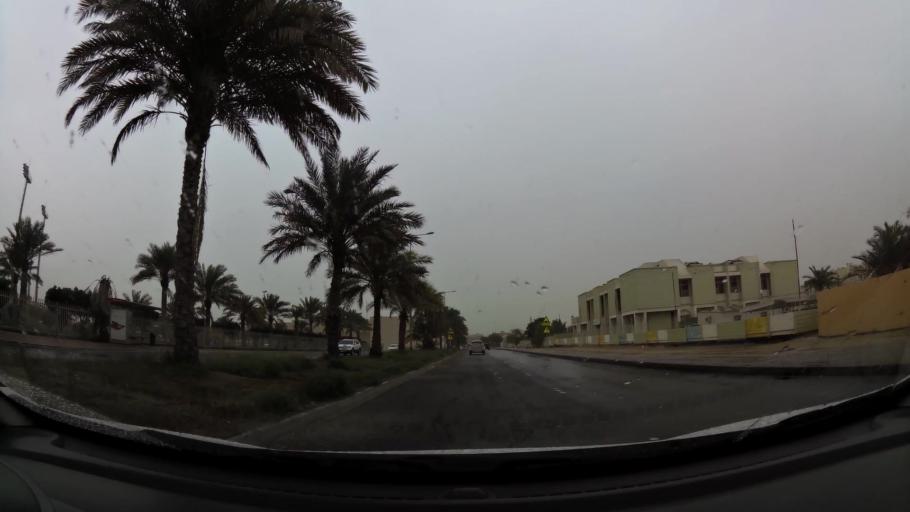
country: BH
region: Northern
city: Madinat `Isa
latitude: 26.1744
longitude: 50.5501
